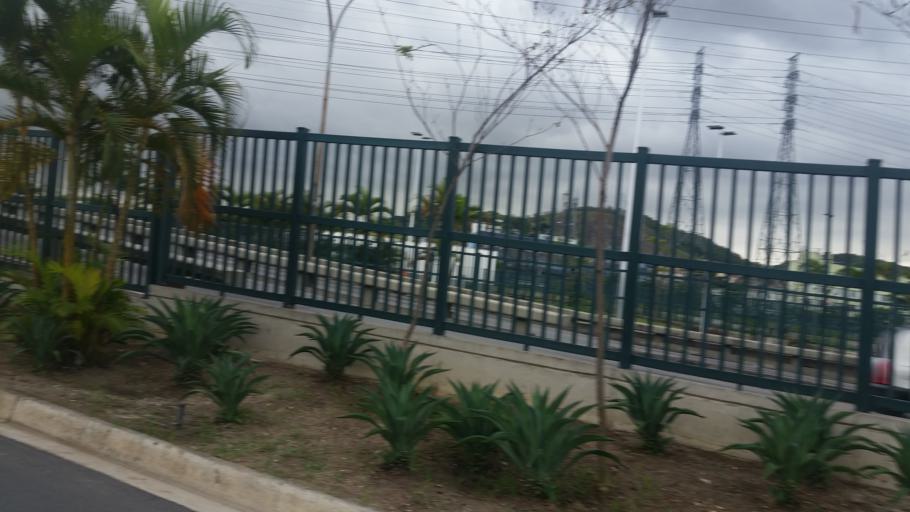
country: BR
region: Rio de Janeiro
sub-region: Sao Joao De Meriti
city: Sao Joao de Meriti
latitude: -22.8607
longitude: -43.3482
